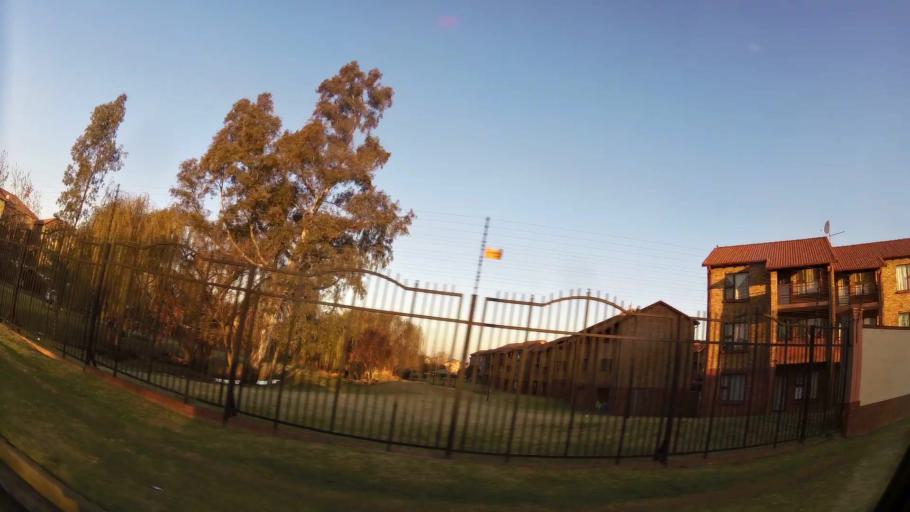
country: ZA
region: Gauteng
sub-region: Ekurhuleni Metropolitan Municipality
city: Germiston
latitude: -26.2570
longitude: 28.1658
